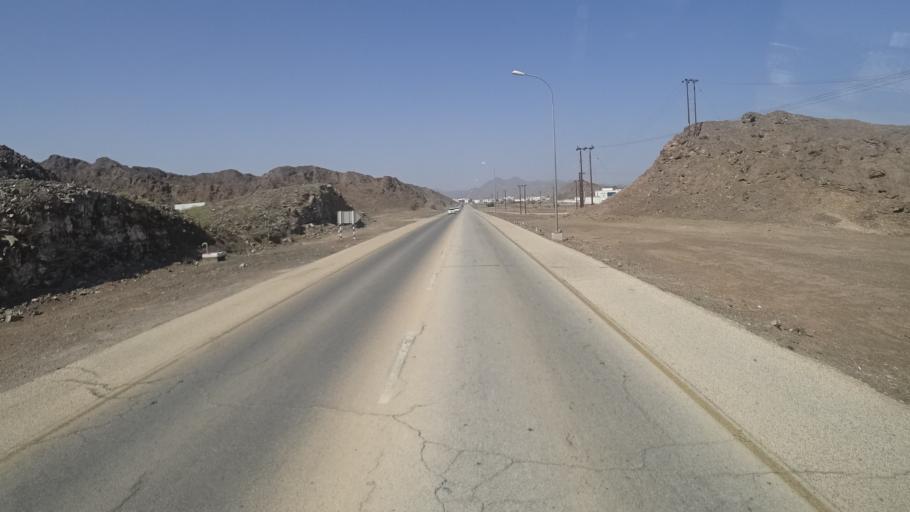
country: OM
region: Ash Sharqiyah
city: Ibra'
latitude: 22.6837
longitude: 58.5655
